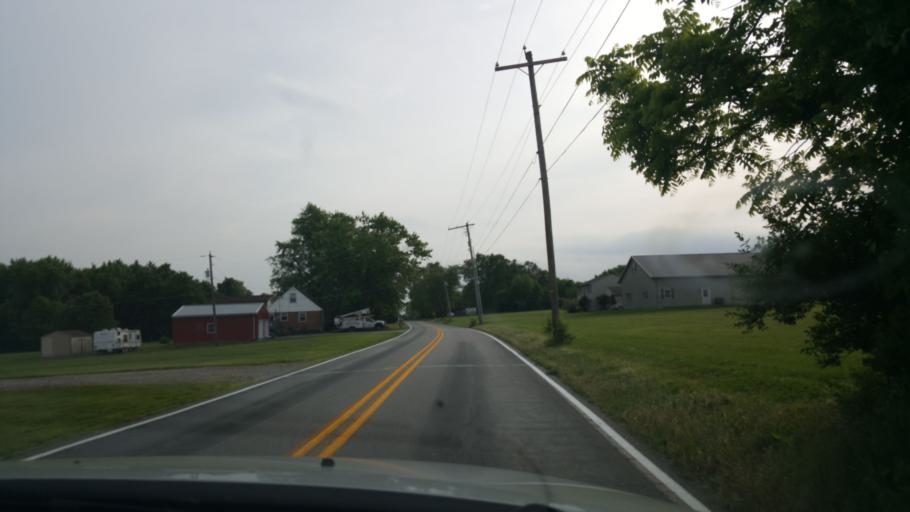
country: US
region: Pennsylvania
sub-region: York County
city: Dover
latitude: 39.9771
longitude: -76.8955
